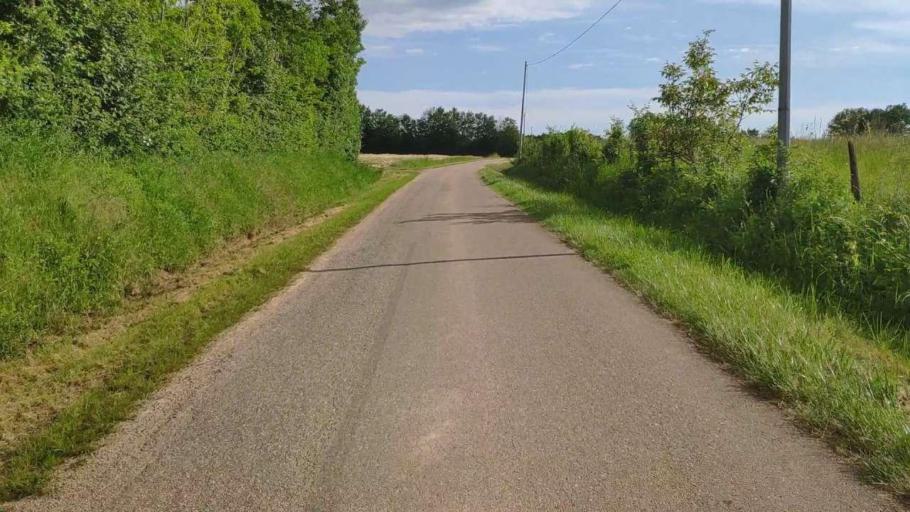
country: FR
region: Bourgogne
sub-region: Departement de Saone-et-Loire
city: Saint-Germain-du-Bois
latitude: 46.7960
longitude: 5.3331
